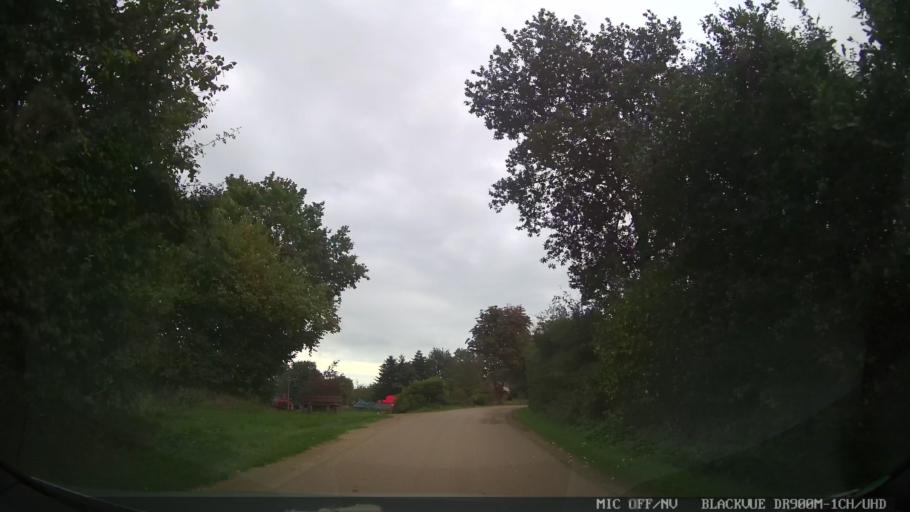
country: DE
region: Schleswig-Holstein
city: Gromitz
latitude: 54.1866
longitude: 10.9541
